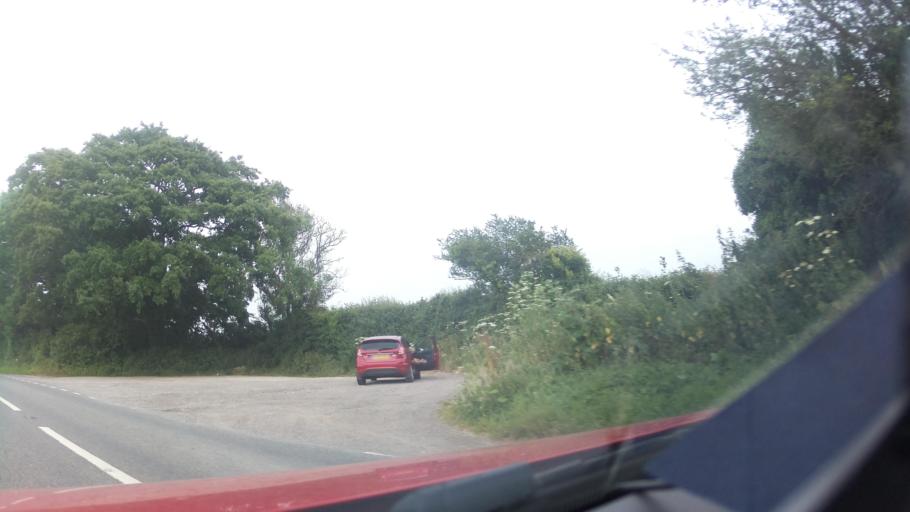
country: GB
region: England
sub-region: Dorset
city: Lyme Regis
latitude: 50.7212
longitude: -2.9627
